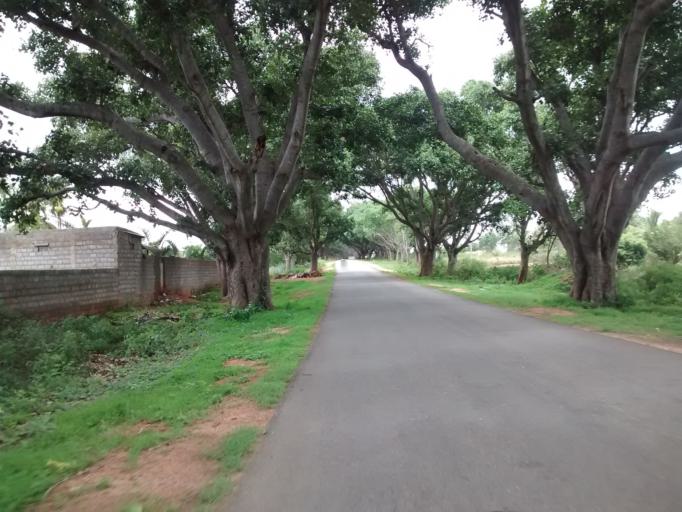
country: IN
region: Karnataka
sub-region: Tumkur
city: Kunigal
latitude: 13.1223
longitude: 77.1546
